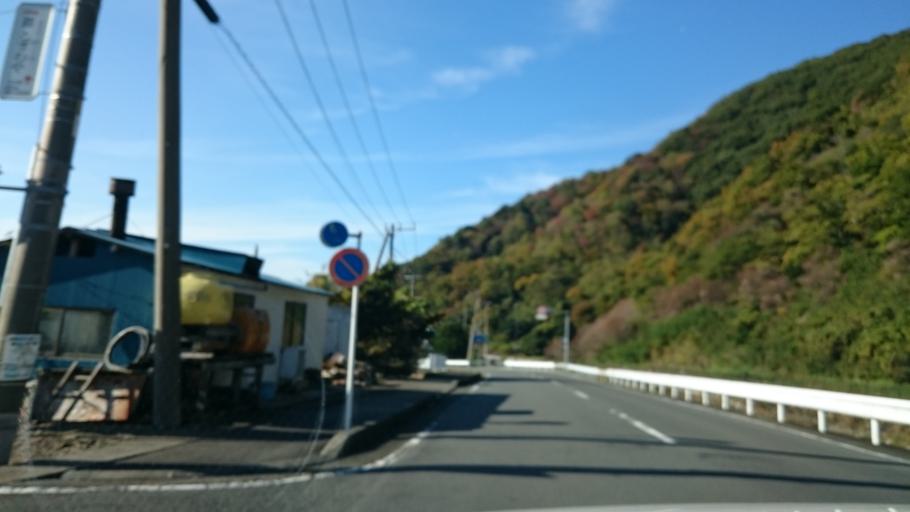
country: JP
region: Shizuoka
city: Heda
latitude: 34.9706
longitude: 138.7950
